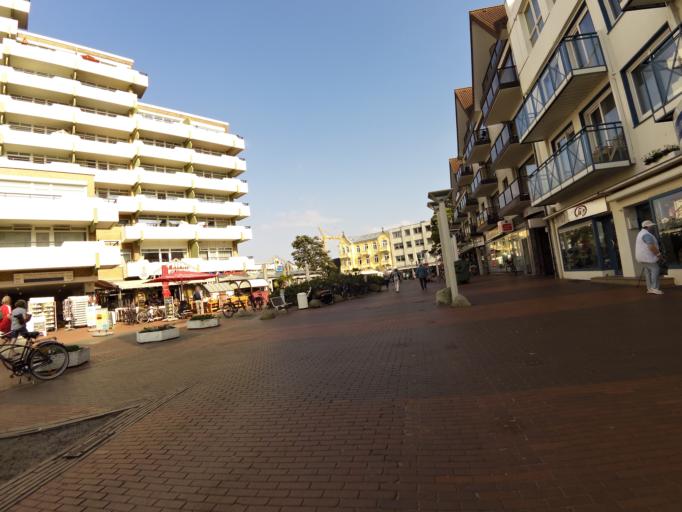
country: DE
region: Lower Saxony
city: Cuxhaven
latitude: 53.8855
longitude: 8.6407
